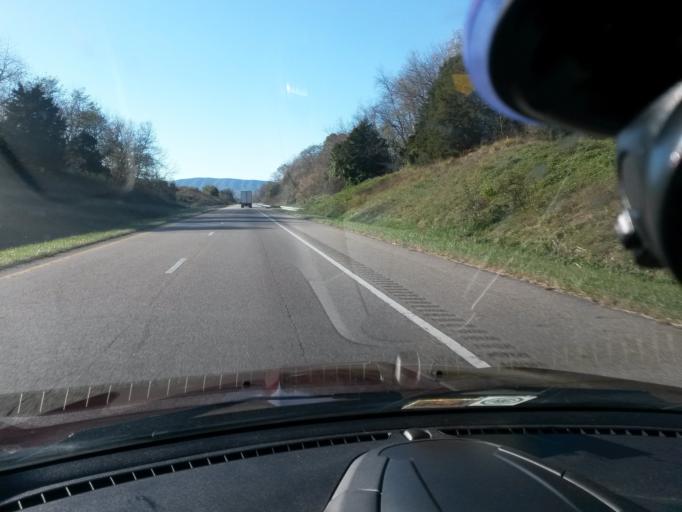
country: US
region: Virginia
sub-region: Rockbridge County
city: East Lexington
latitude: 37.8461
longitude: -79.4606
